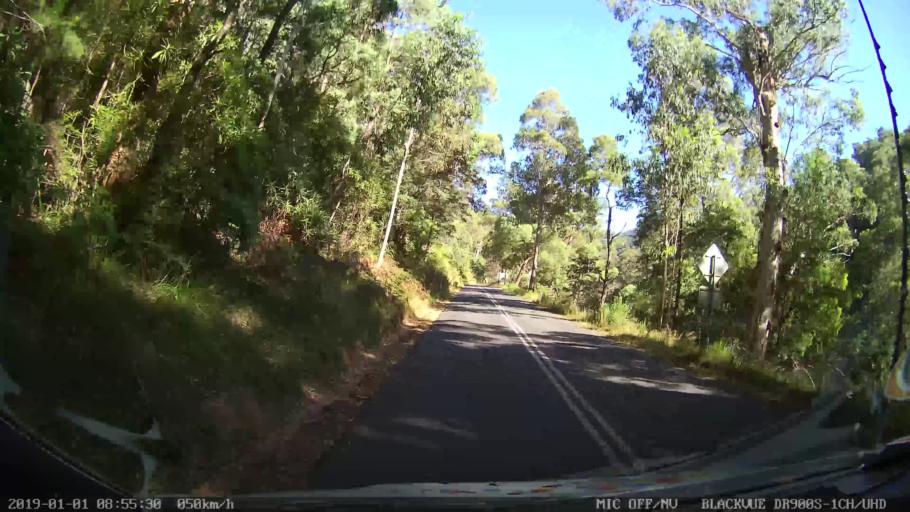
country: AU
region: New South Wales
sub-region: Snowy River
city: Jindabyne
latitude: -36.2535
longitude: 148.1918
